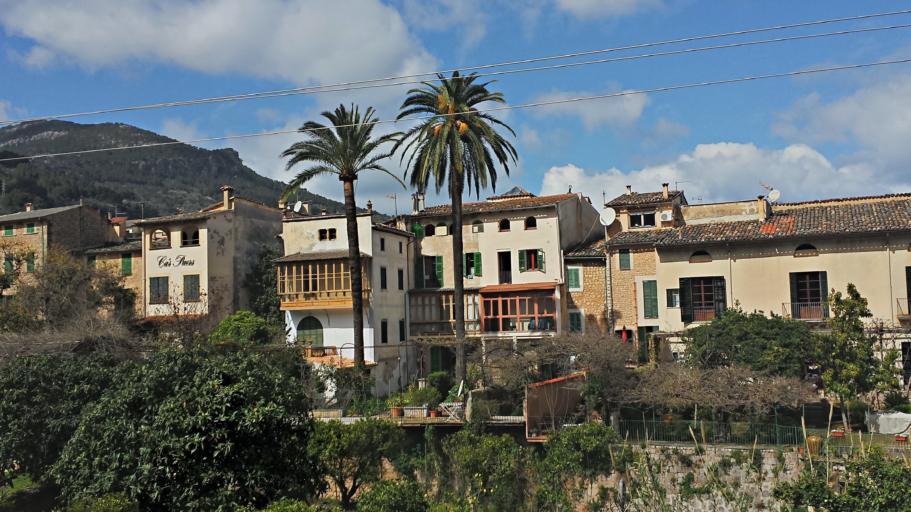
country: ES
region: Balearic Islands
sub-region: Illes Balears
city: Soller
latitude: 39.7647
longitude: 2.7149
